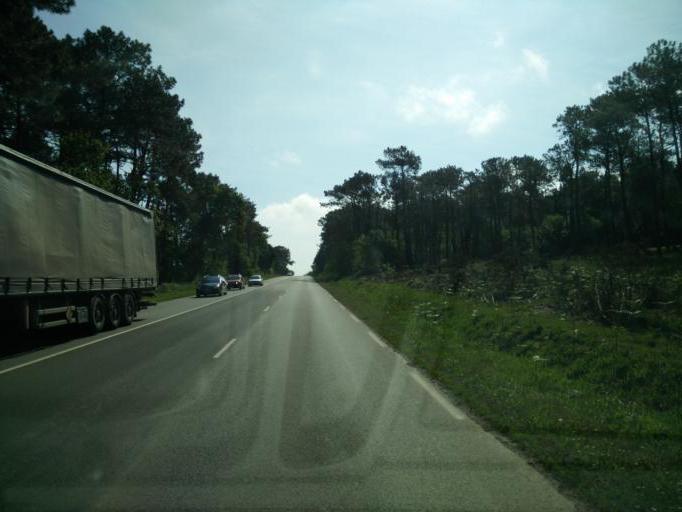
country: FR
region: Brittany
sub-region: Departement du Finistere
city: Lanveoc
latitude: 48.2480
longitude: -4.4435
